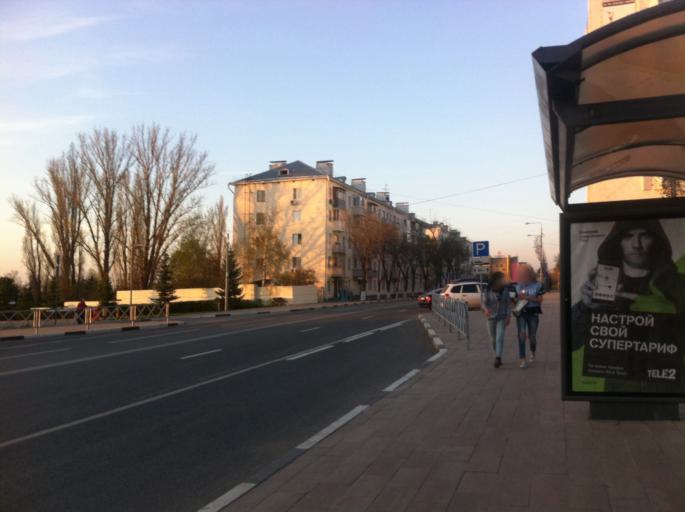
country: RU
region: Samara
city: Samara
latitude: 53.2026
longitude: 50.1114
